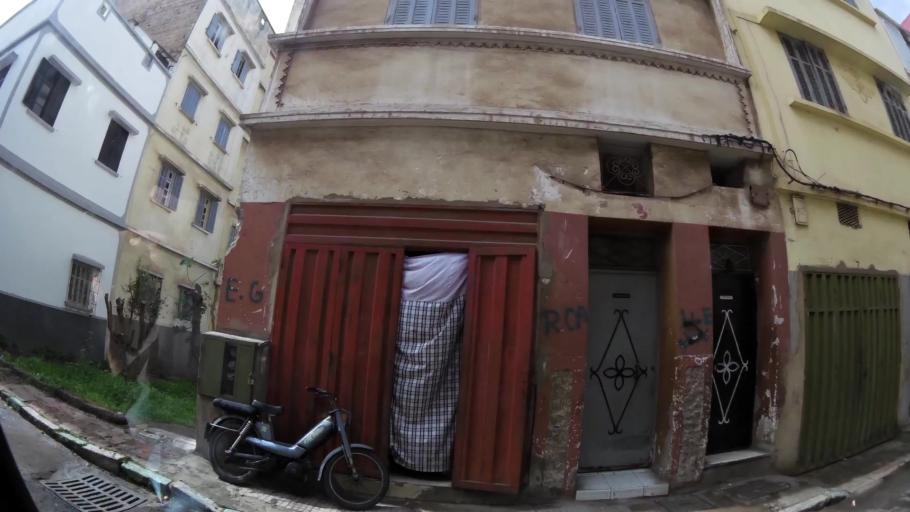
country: MA
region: Grand Casablanca
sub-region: Casablanca
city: Casablanca
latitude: 33.5450
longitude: -7.5682
